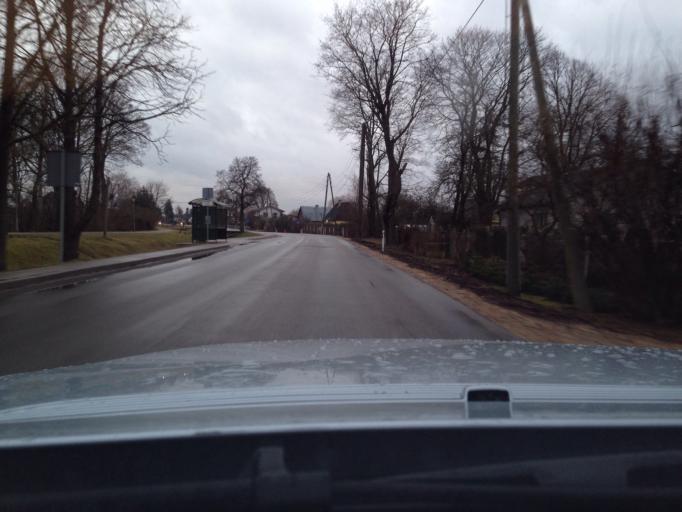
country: LV
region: Marupe
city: Marupe
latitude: 56.8987
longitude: 24.0464
